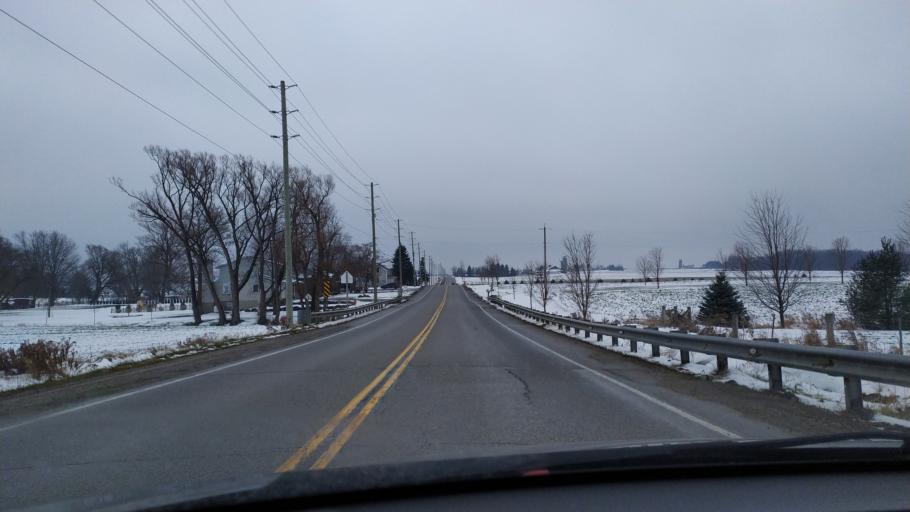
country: CA
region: Ontario
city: Waterloo
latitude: 43.5147
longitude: -80.6203
